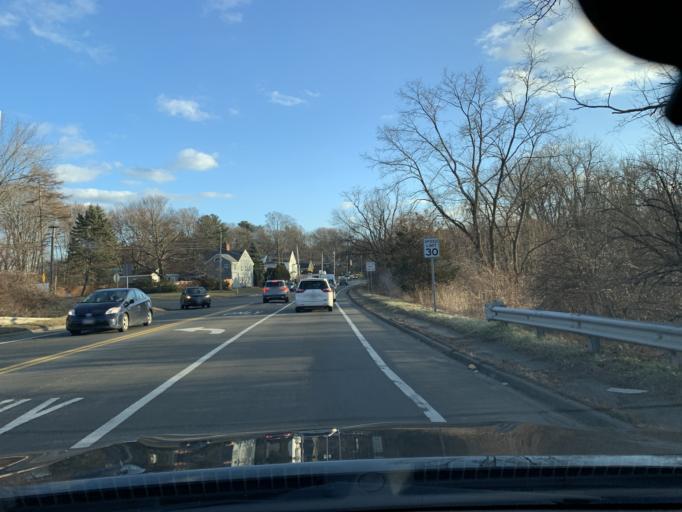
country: US
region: Massachusetts
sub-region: Essex County
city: Danvers
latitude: 42.5785
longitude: -70.9592
